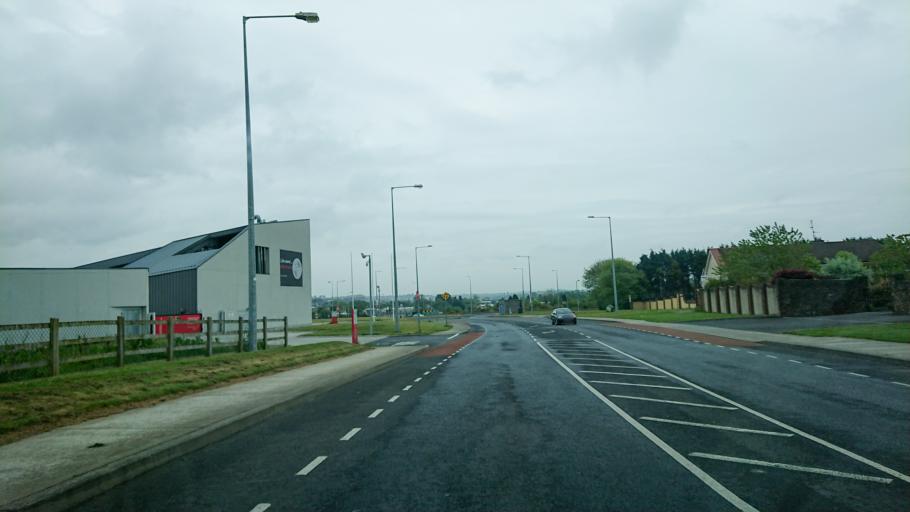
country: IE
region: Munster
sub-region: Waterford
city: Waterford
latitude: 52.2418
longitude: -7.1341
